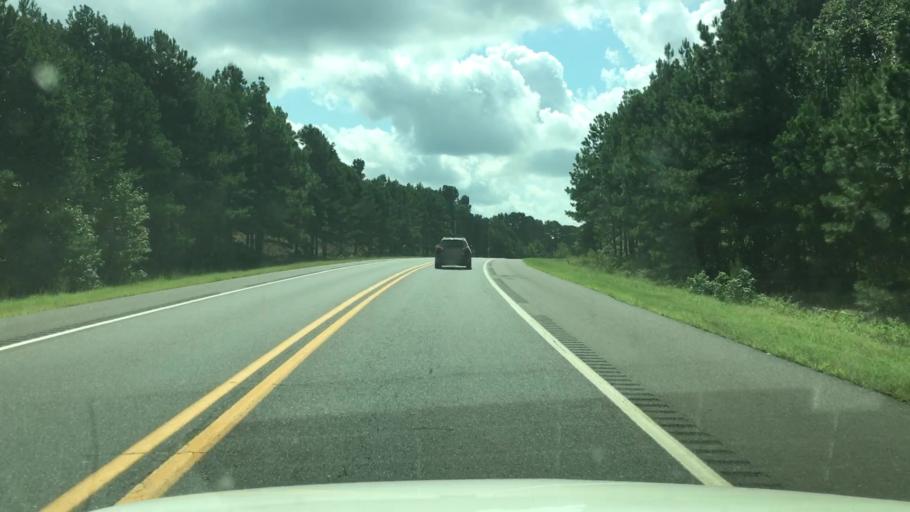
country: US
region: Arkansas
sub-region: Clark County
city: Arkadelphia
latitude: 34.2297
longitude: -93.0938
